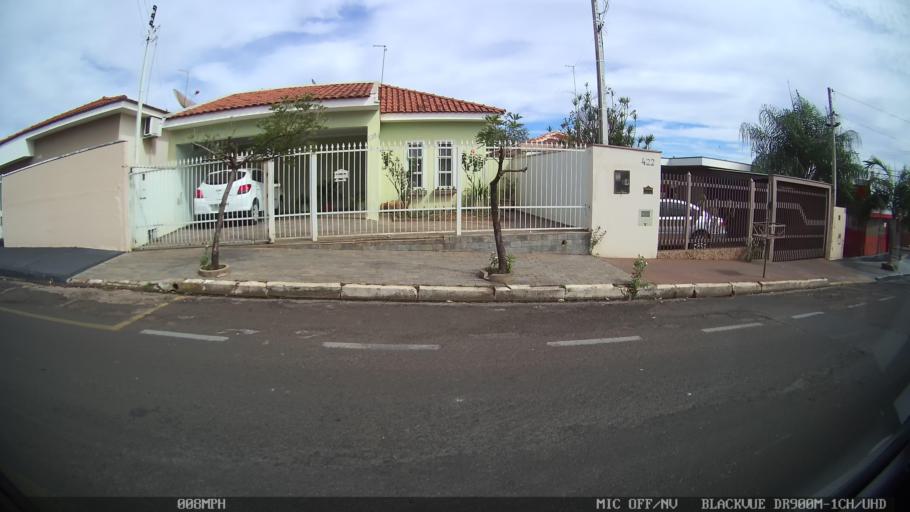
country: BR
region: Sao Paulo
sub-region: Catanduva
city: Catanduva
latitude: -21.1462
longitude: -48.9690
